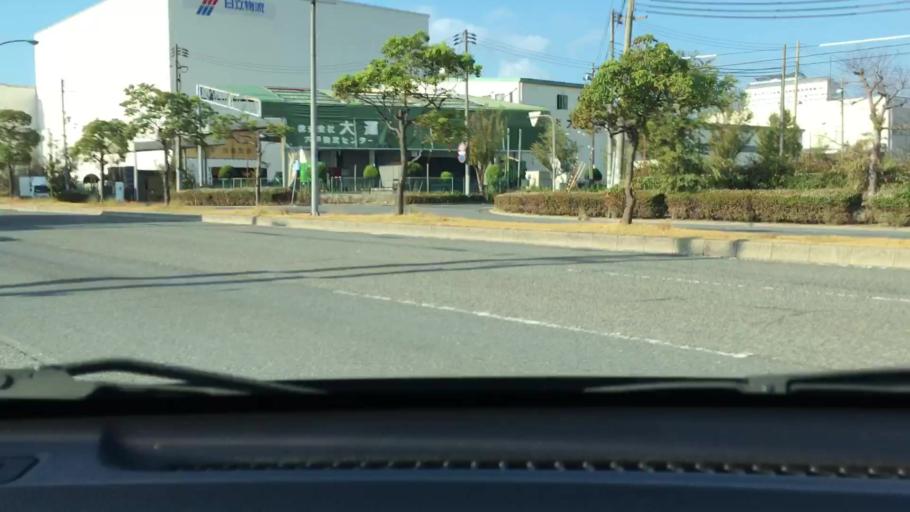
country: JP
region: Hyogo
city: Ashiya
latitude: 34.6924
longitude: 135.2772
